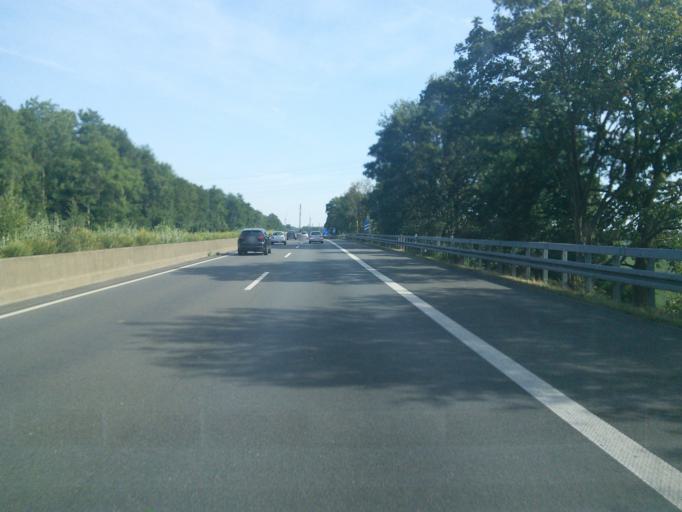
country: DE
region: North Rhine-Westphalia
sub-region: Regierungsbezirk Dusseldorf
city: Dormagen
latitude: 51.0884
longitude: 6.8095
